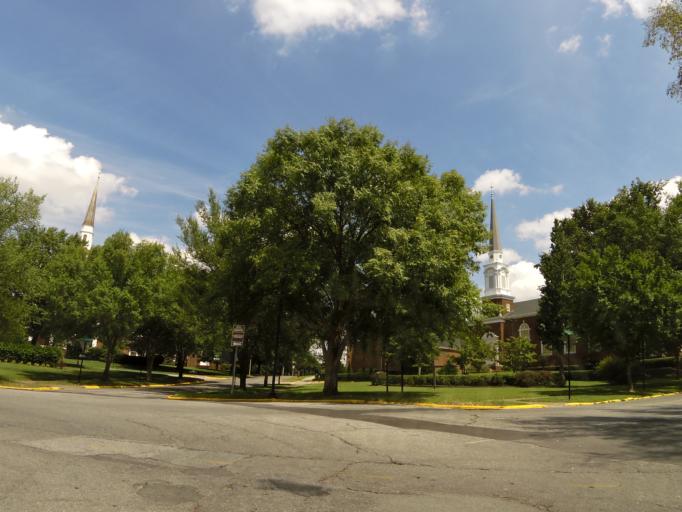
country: US
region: Tennessee
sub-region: Sullivan County
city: Kingsport
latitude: 36.5490
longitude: -82.5583
